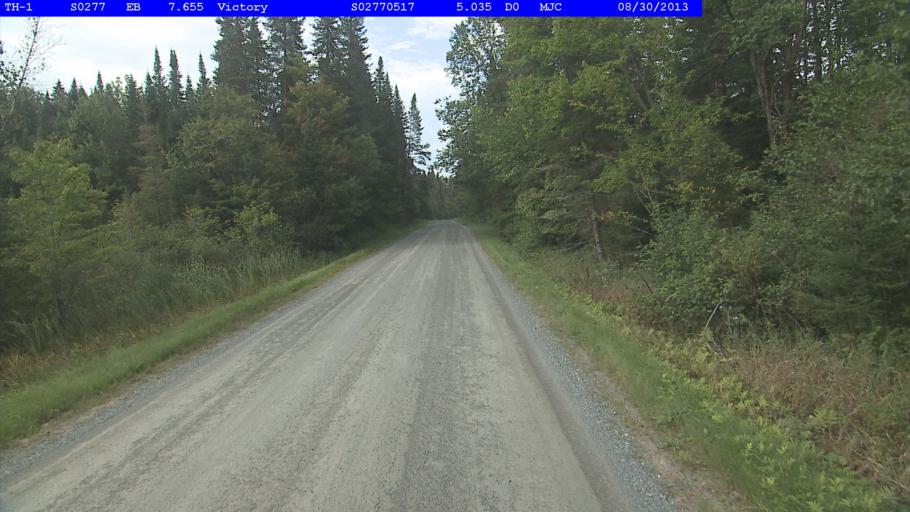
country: US
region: Vermont
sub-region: Caledonia County
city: Lyndonville
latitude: 44.5418
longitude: -71.7869
